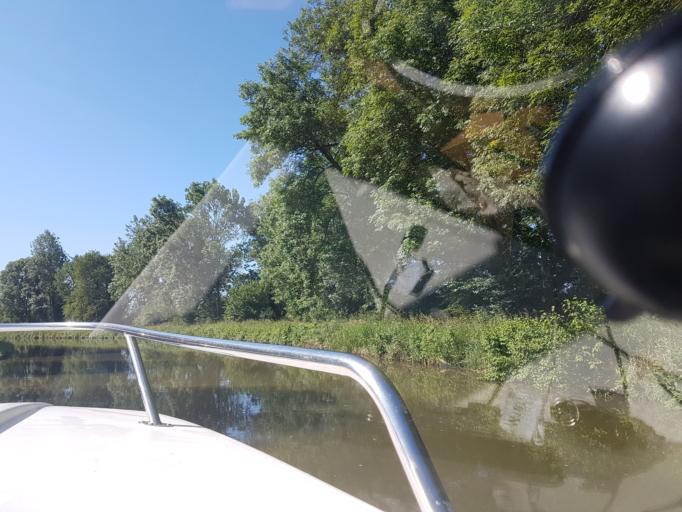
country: FR
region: Bourgogne
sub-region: Departement de la Nievre
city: Clamecy
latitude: 47.5350
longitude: 3.5995
